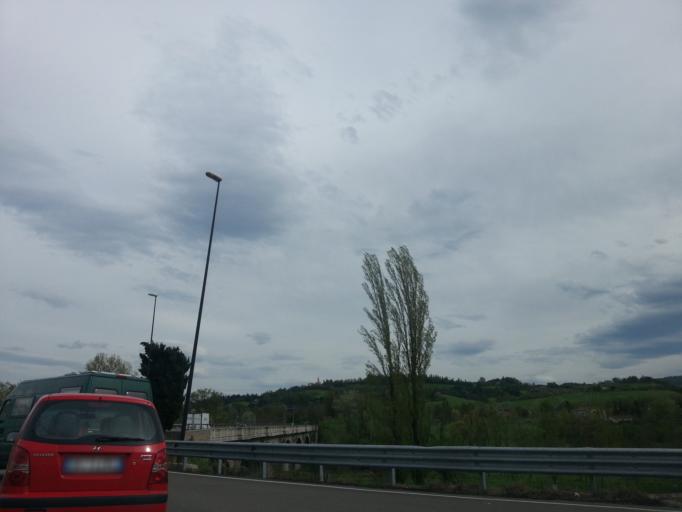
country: IT
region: Emilia-Romagna
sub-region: Provincia di Reggio Emilia
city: Puianello
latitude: 44.6246
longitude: 10.5665
